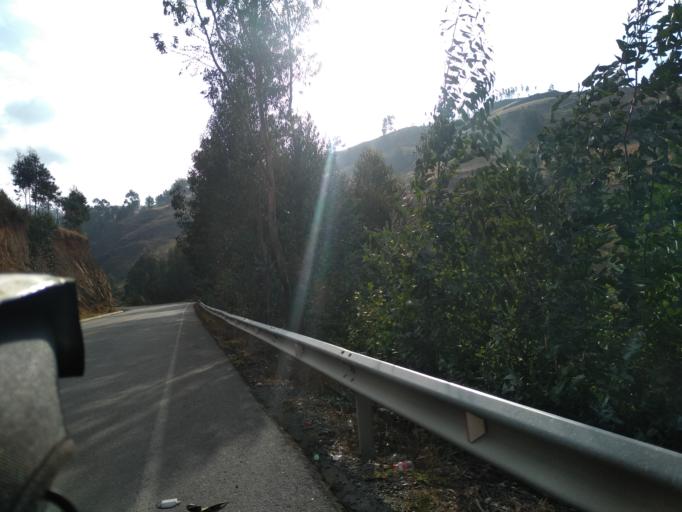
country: PE
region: La Libertad
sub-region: Provincia de Otuzco
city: Agallpampa
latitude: -7.9900
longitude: -78.5333
